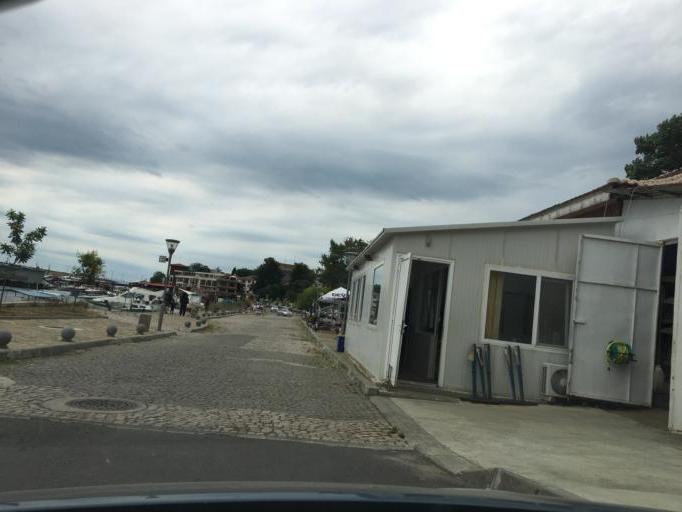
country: BG
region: Burgas
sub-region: Obshtina Sozopol
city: Sozopol
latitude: 42.4191
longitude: 27.6913
